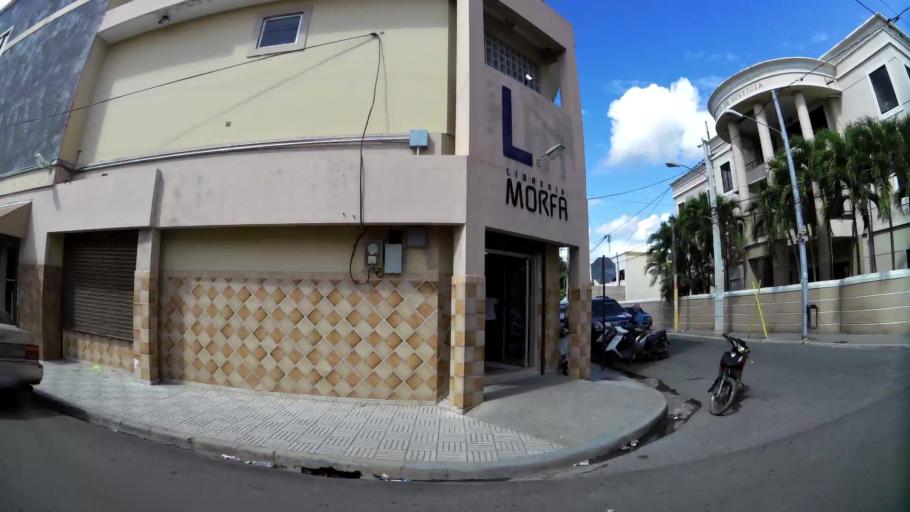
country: DO
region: La Vega
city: Concepcion de La Vega
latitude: 19.2226
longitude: -70.5314
